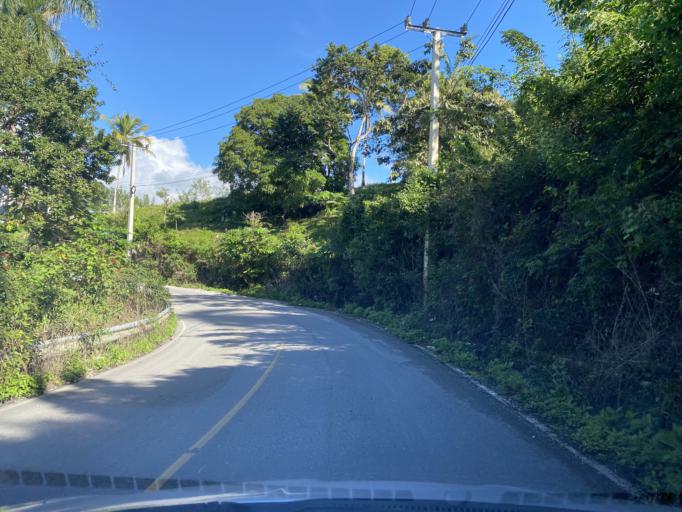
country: DO
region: Samana
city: Sanchez
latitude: 19.2498
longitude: -69.5927
